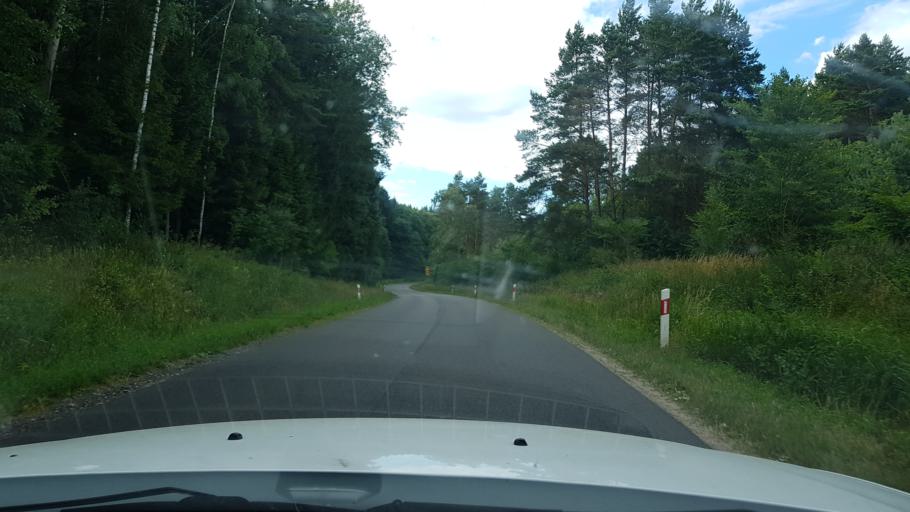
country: PL
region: West Pomeranian Voivodeship
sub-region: Powiat drawski
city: Zlocieniec
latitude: 53.4886
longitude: 16.0408
